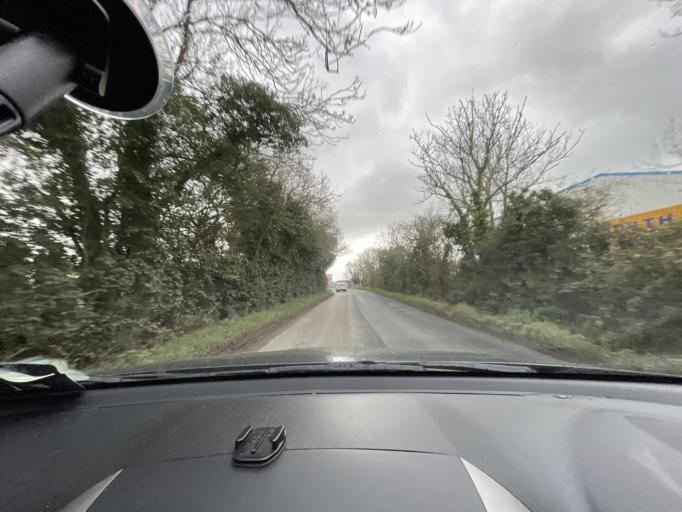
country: IE
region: Leinster
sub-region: Lu
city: Drogheda
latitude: 53.7245
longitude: -6.3216
